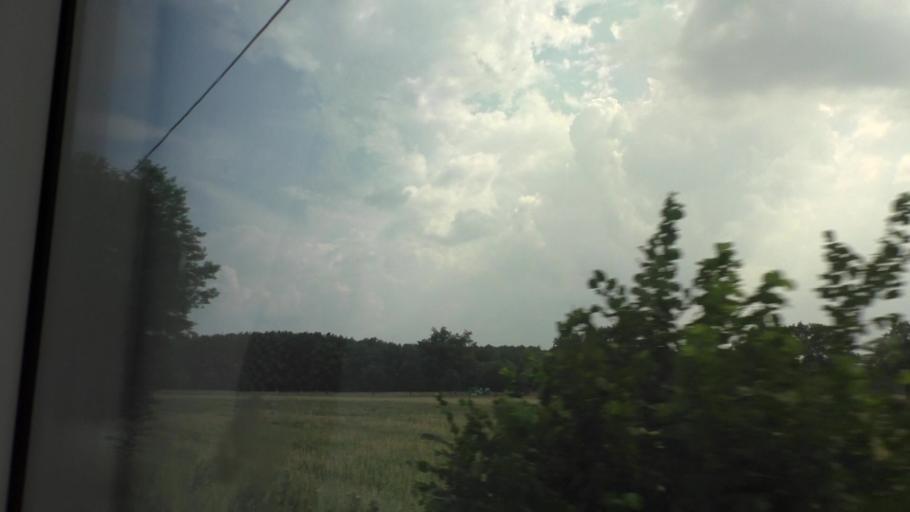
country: DE
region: Brandenburg
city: Storkow
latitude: 52.2732
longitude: 13.8782
